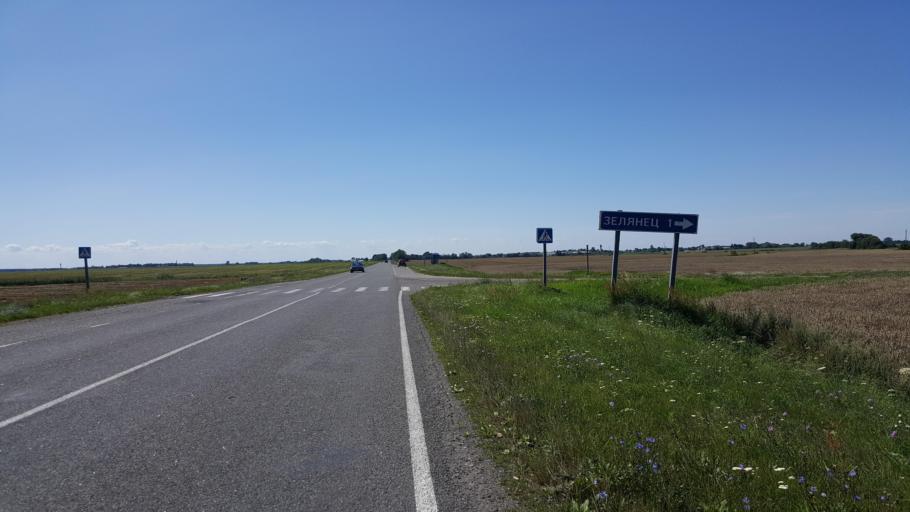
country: BY
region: Brest
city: Charnawchytsy
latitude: 52.2071
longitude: 23.7920
